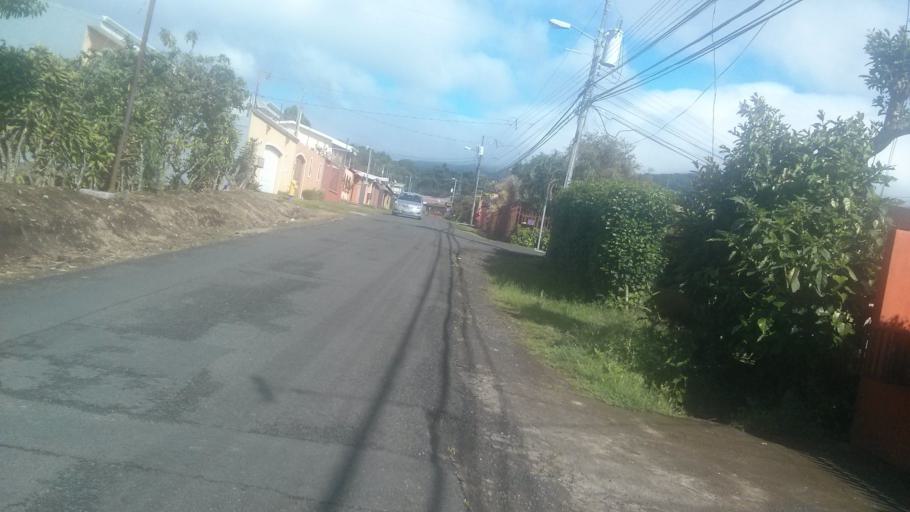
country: CR
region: Heredia
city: Angeles
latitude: 10.0164
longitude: -84.0475
